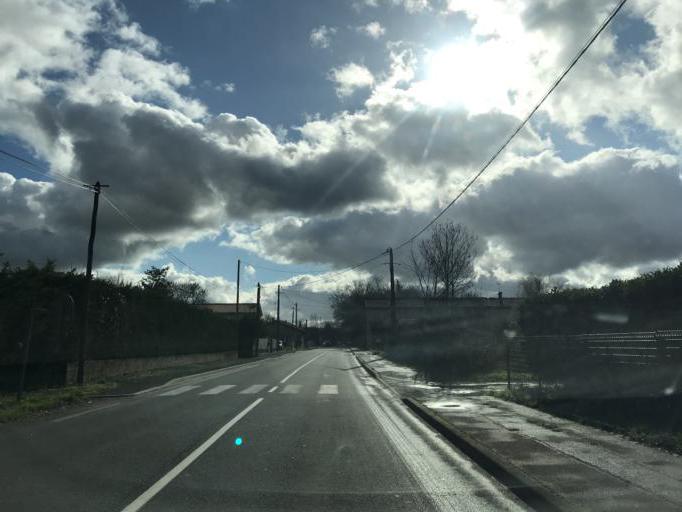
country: FR
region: Rhone-Alpes
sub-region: Departement de l'Ain
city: Reyrieux
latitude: 45.9492
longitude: 4.8081
